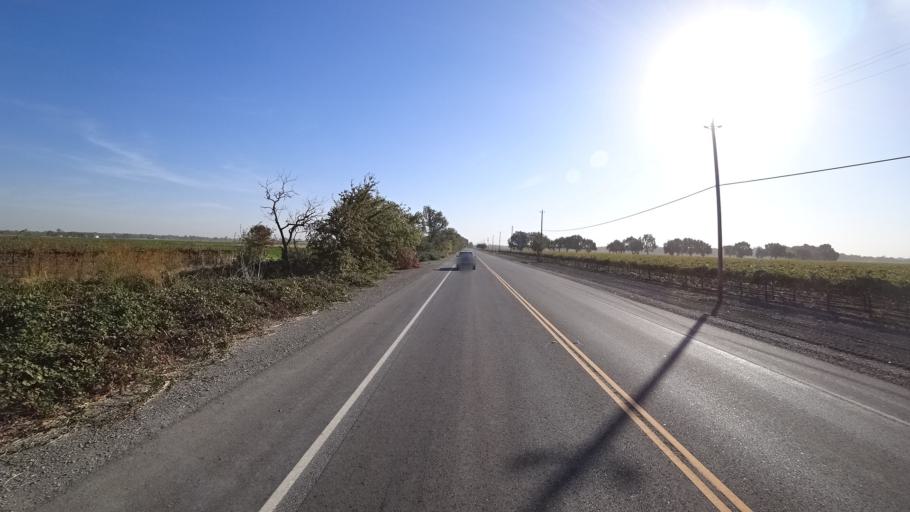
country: US
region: California
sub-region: Sacramento County
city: Parkway
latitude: 38.4144
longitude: -121.5533
